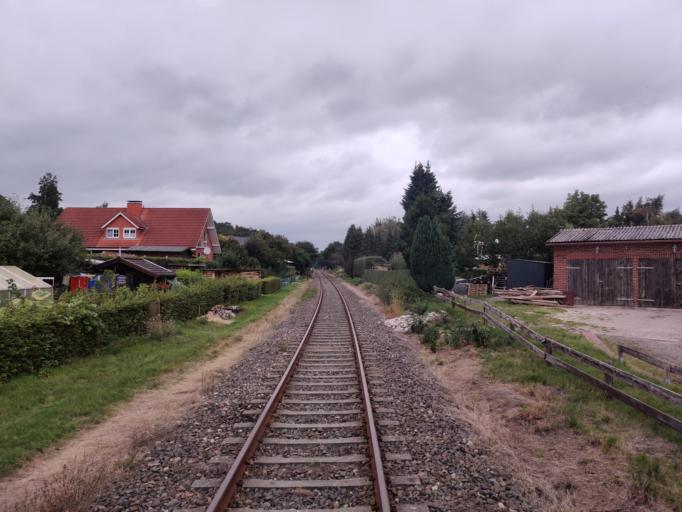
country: DE
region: Lower Saxony
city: Gnarrenburg
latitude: 53.3942
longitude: 9.0153
